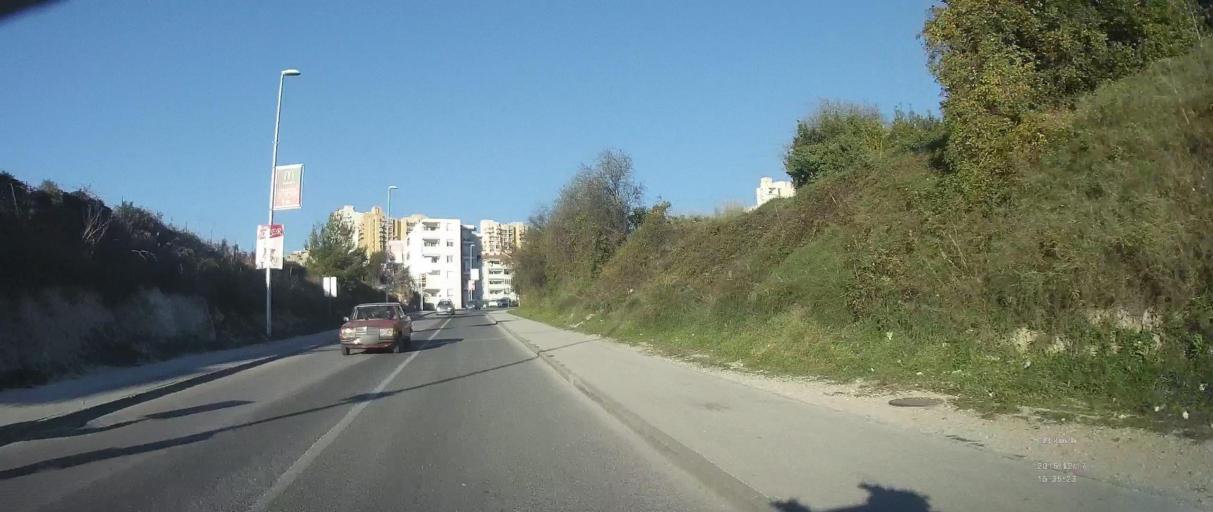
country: HR
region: Splitsko-Dalmatinska
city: Vranjic
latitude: 43.5043
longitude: 16.4779
